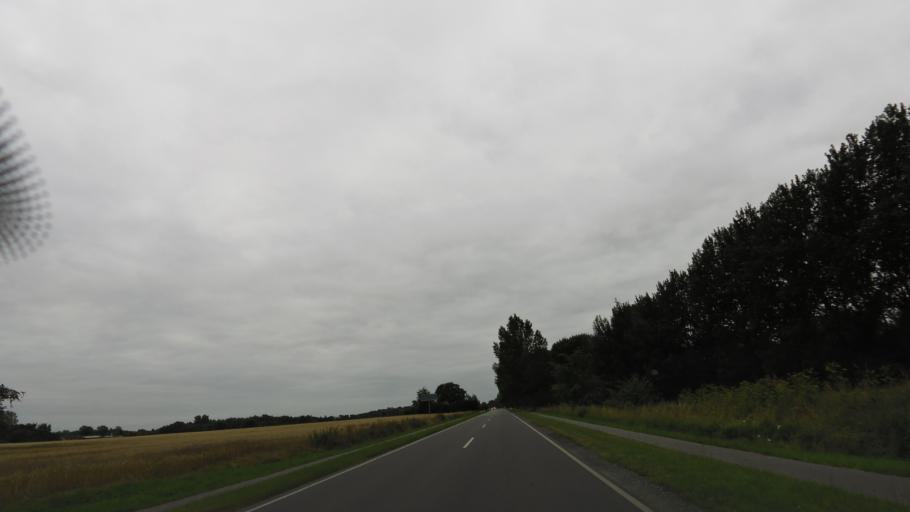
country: DK
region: South Denmark
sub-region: Nordfyns Kommune
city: Otterup
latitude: 55.5498
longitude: 10.4421
